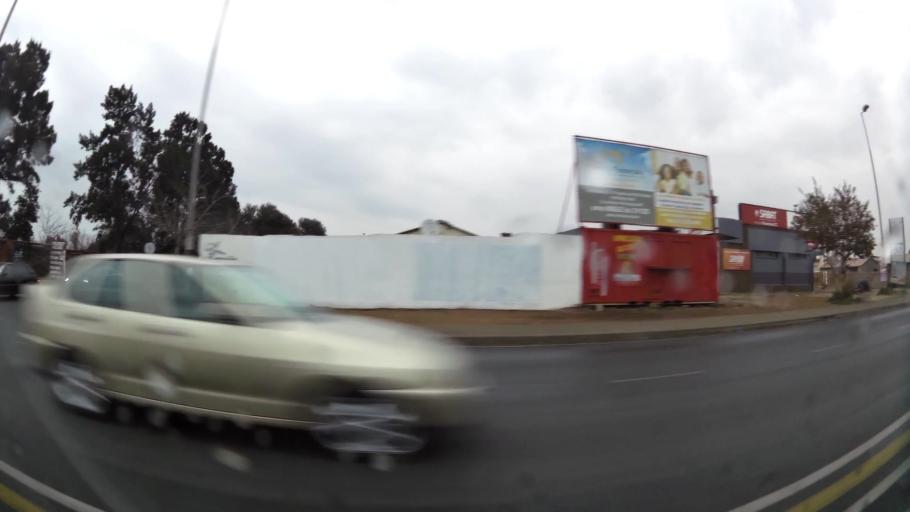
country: ZA
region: Gauteng
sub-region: City of Johannesburg Metropolitan Municipality
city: Soweto
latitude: -26.2628
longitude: 27.8572
